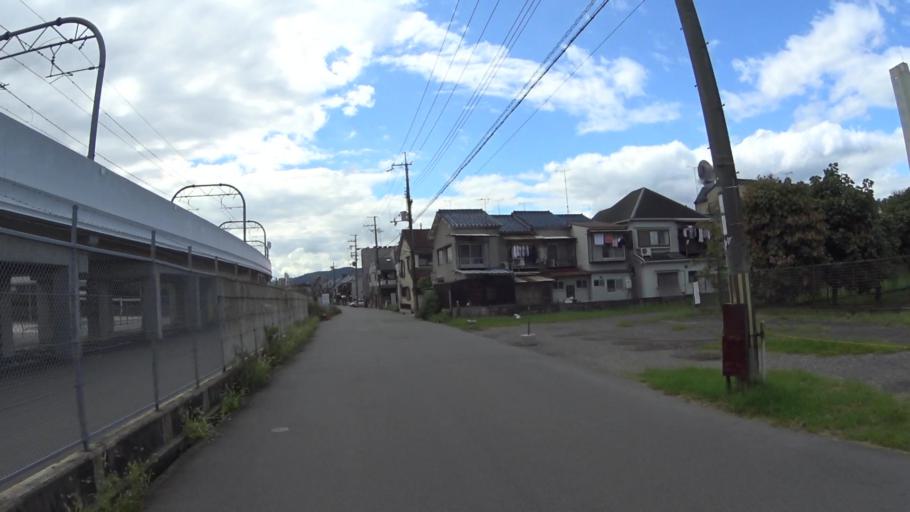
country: JP
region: Kyoto
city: Yawata
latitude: 34.9095
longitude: 135.7271
